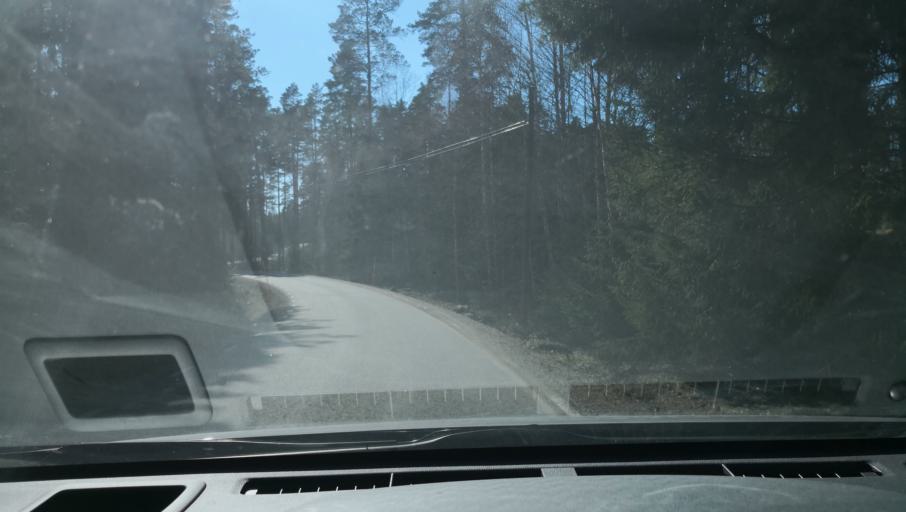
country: SE
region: Vaestmanland
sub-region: Sala Kommun
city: Sala
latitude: 59.9284
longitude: 16.4540
